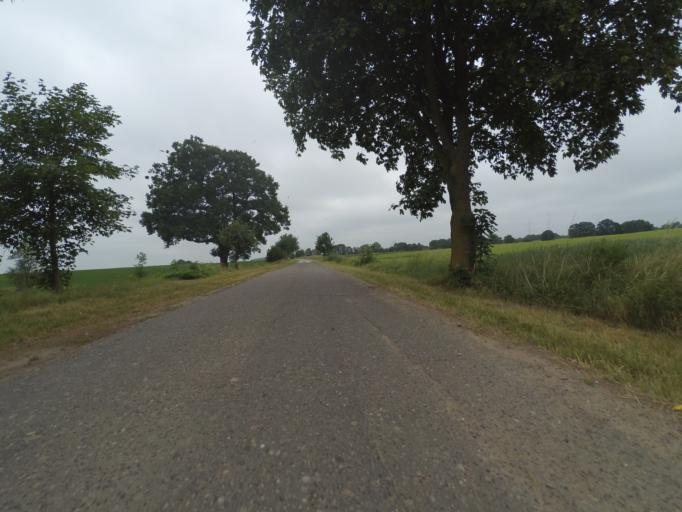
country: DE
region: Mecklenburg-Vorpommern
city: Plau am See
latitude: 53.4689
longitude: 12.2508
